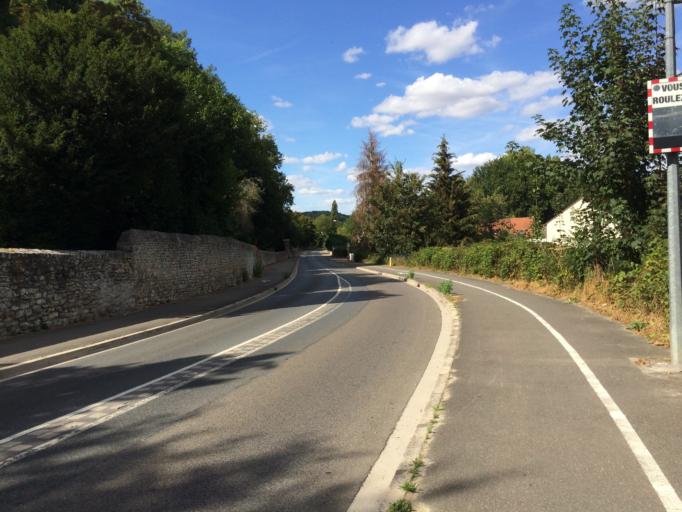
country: FR
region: Ile-de-France
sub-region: Departement de l'Essonne
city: La Ferte-Alais
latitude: 48.4774
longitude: 2.3449
